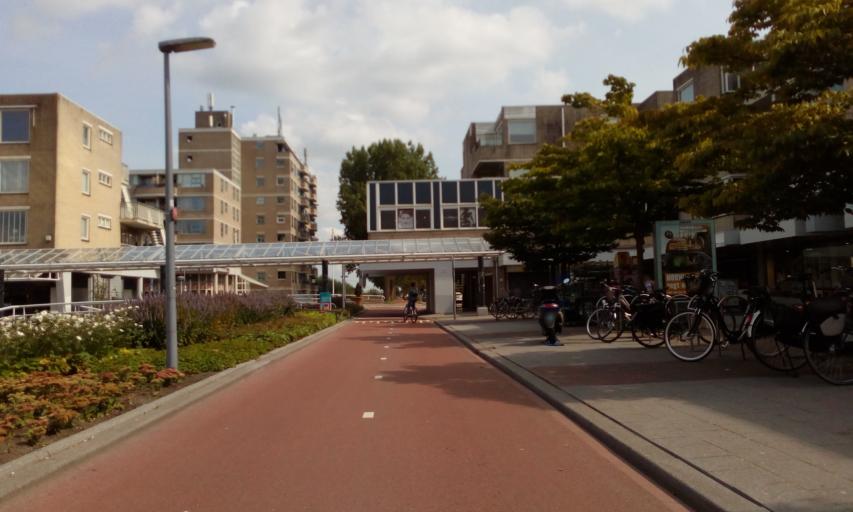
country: NL
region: South Holland
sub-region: Gemeente Capelle aan den IJssel
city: Capelle aan den IJssel
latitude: 51.9651
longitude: 4.5710
